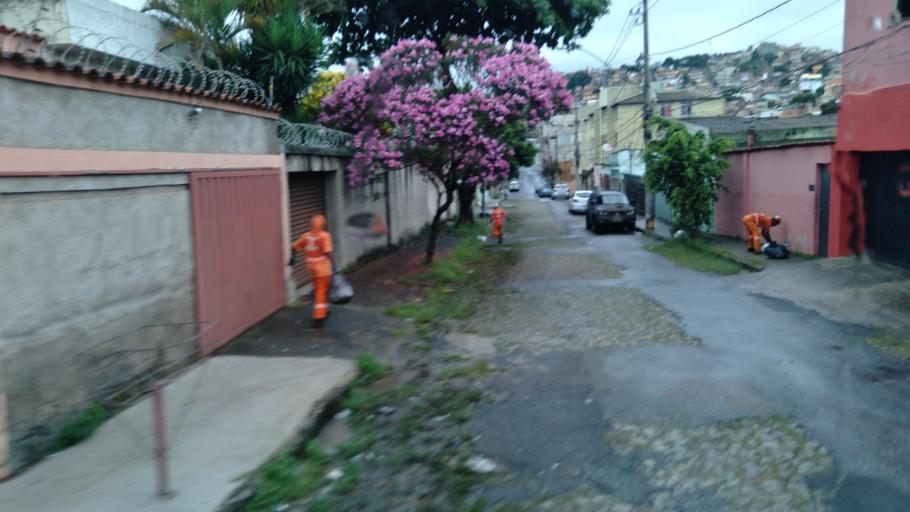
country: BR
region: Minas Gerais
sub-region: Belo Horizonte
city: Belo Horizonte
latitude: -19.9161
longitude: -43.9018
